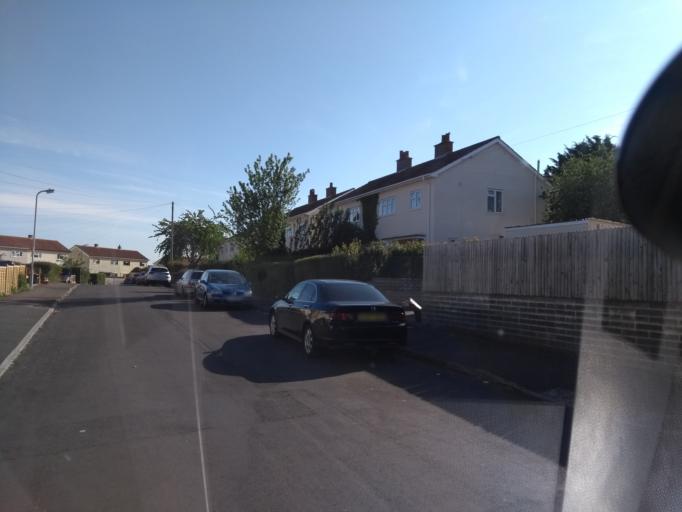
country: GB
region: England
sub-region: Somerset
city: Taunton
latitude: 51.0113
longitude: -3.0856
